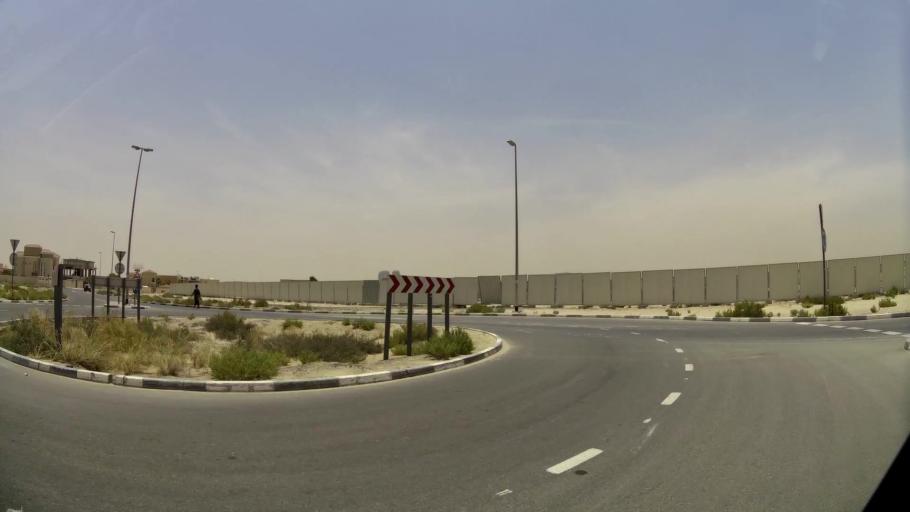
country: AE
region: Dubai
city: Dubai
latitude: 25.0915
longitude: 55.2301
